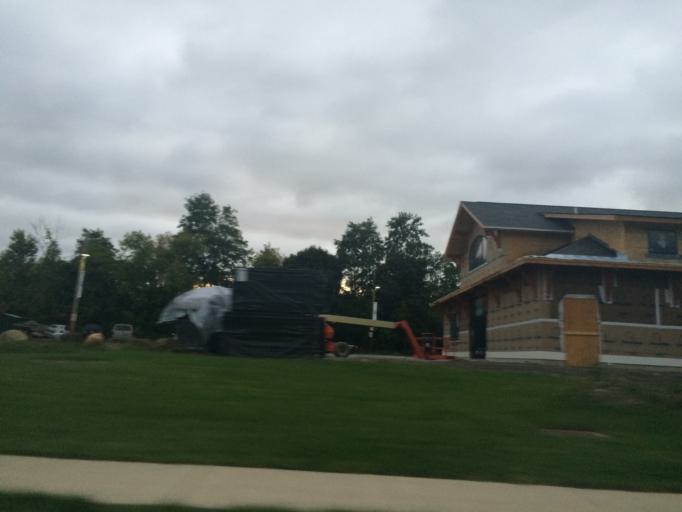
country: US
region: New York
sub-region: Erie County
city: East Aurora
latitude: 42.7693
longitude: -78.6115
